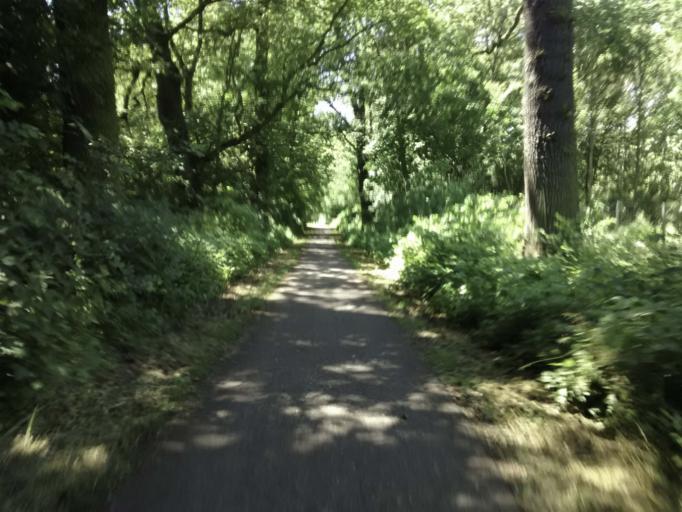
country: DE
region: Saxony-Anhalt
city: Dessau
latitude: 51.8635
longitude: 12.2838
